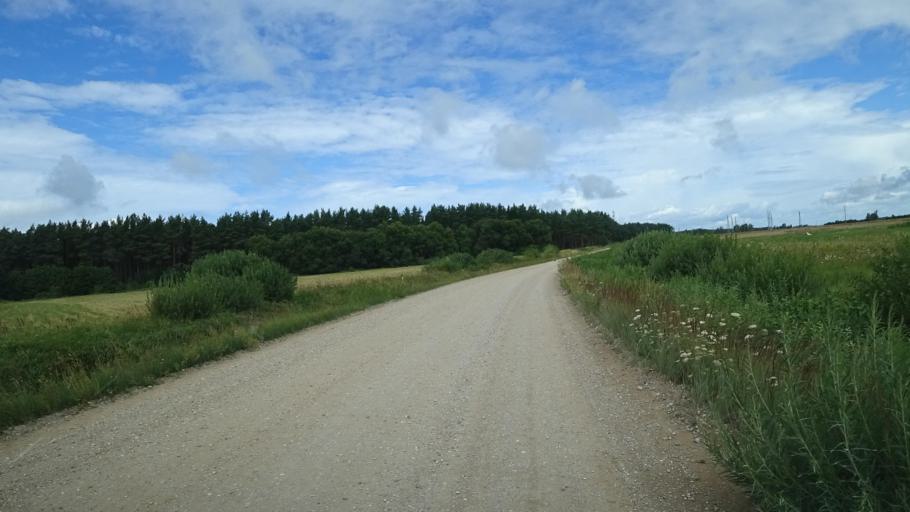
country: LV
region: Liepaja
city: Vec-Liepaja
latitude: 56.6331
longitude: 21.0472
